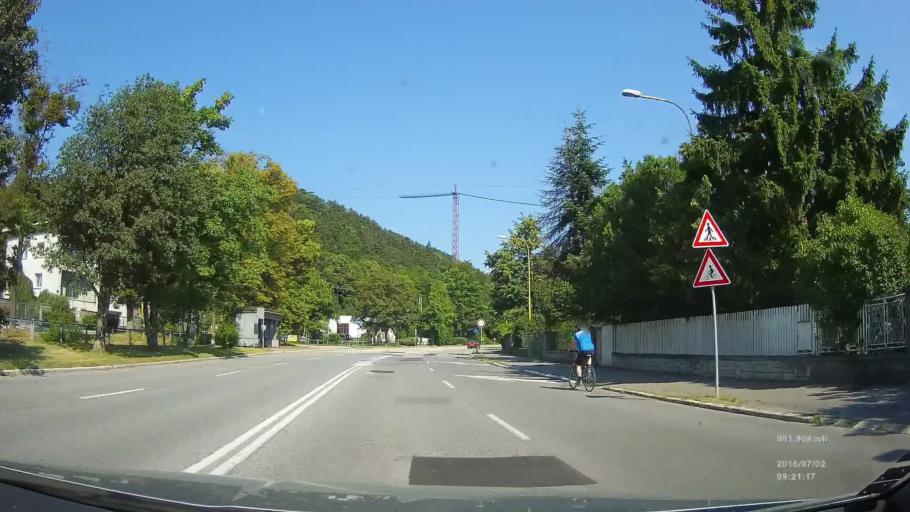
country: SK
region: Kosicky
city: Kosice
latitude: 48.7421
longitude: 21.2389
